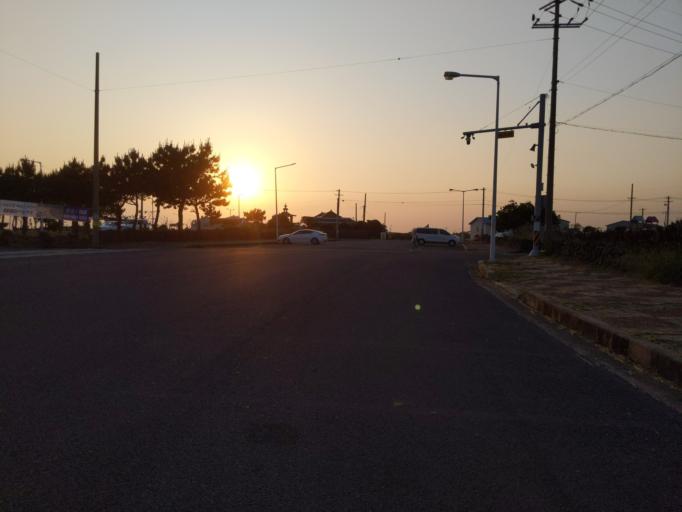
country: KR
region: Jeju-do
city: Gaigeturi
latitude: 33.2210
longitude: 126.2475
